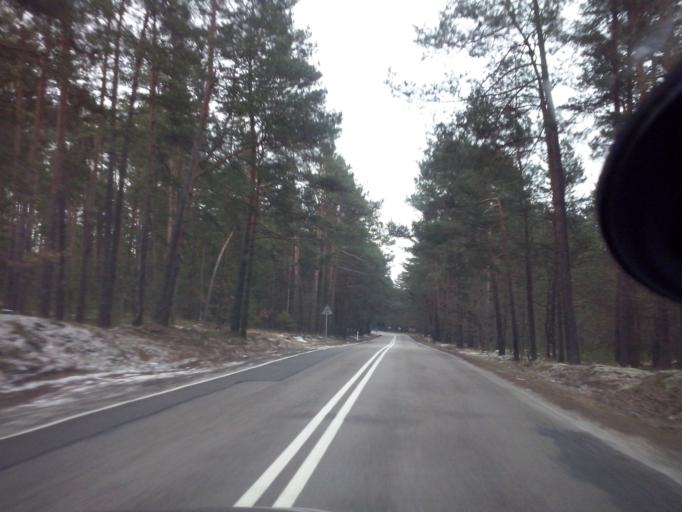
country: PL
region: Subcarpathian Voivodeship
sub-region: Powiat nizanski
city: Harasiuki
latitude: 50.5053
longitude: 22.5784
